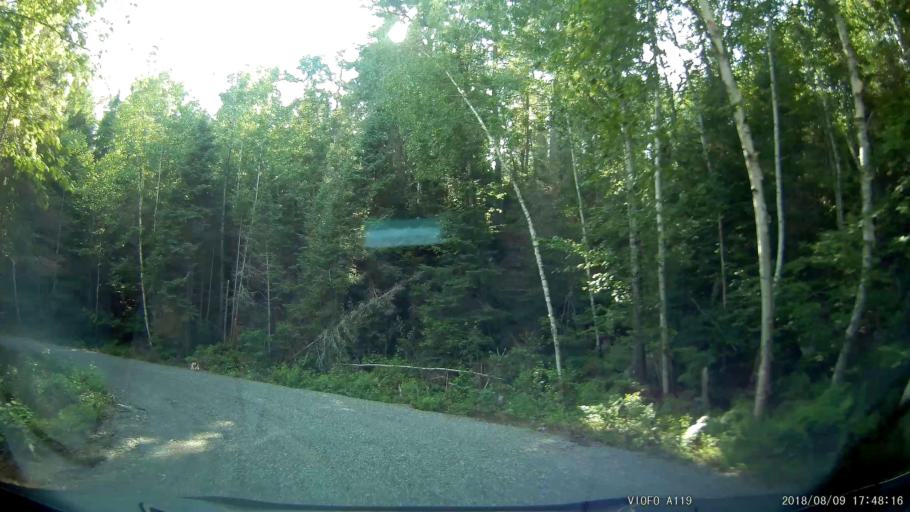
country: CA
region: Ontario
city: Rayside-Balfour
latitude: 46.5909
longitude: -81.5401
